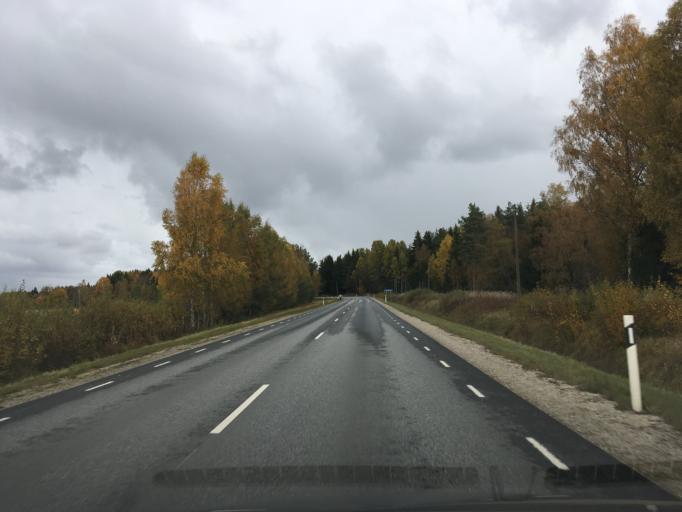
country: EE
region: Harju
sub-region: Anija vald
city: Kehra
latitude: 59.3162
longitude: 25.3437
